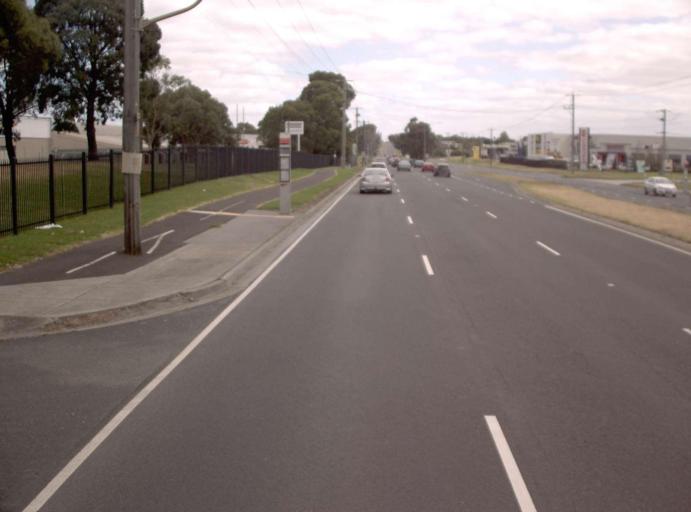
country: AU
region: Victoria
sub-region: Knox
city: Scoresby
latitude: -37.9069
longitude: 145.2373
